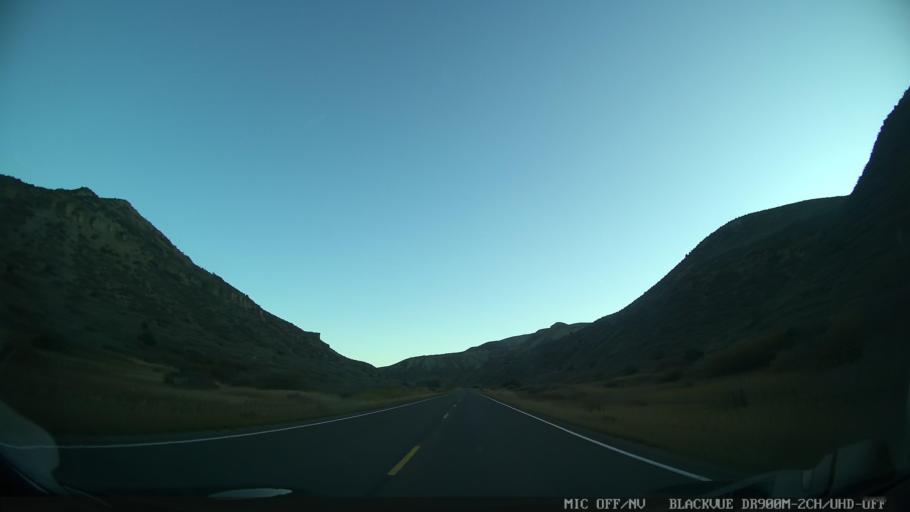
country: US
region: Colorado
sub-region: Eagle County
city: Edwards
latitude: 39.7764
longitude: -106.6825
